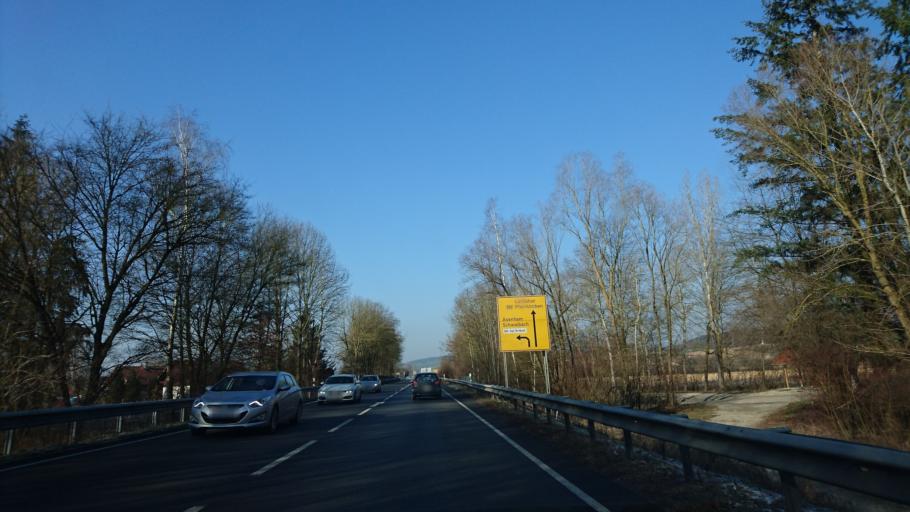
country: DE
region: Bavaria
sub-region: Lower Bavaria
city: Bad Birnbach
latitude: 48.4363
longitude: 13.0755
